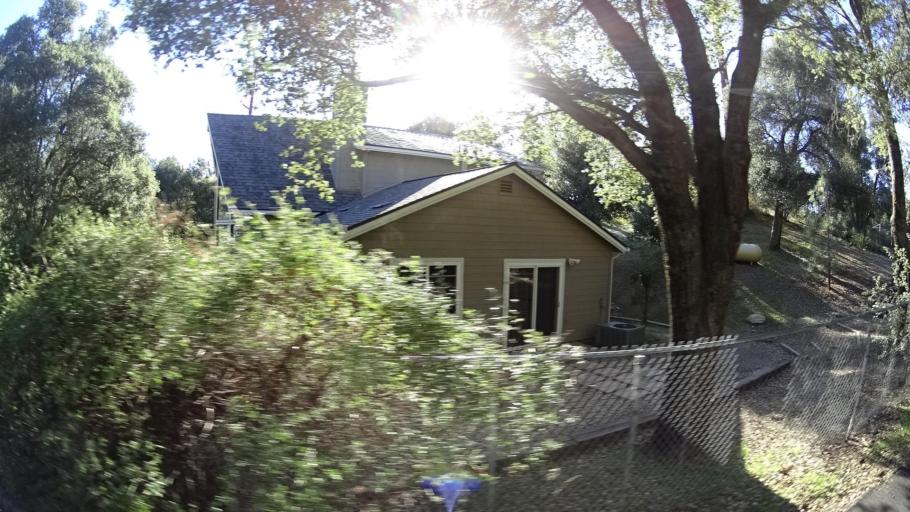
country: US
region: California
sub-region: San Diego County
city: Pine Valley
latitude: 32.8265
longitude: -116.5346
